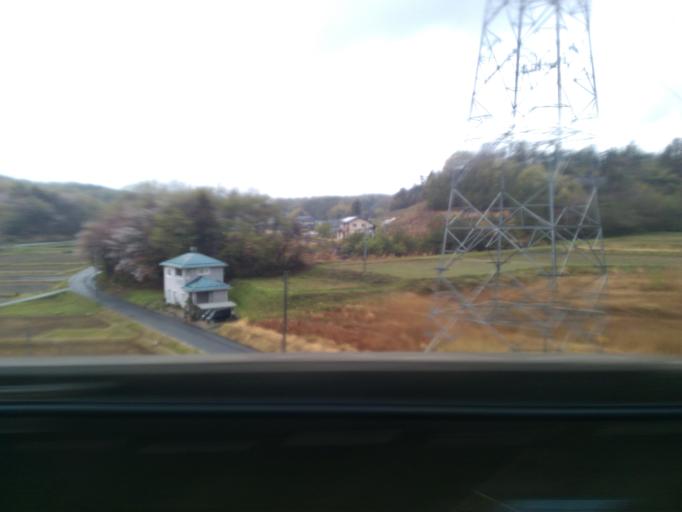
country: JP
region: Fukushima
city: Motomiya
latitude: 37.5117
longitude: 140.4299
